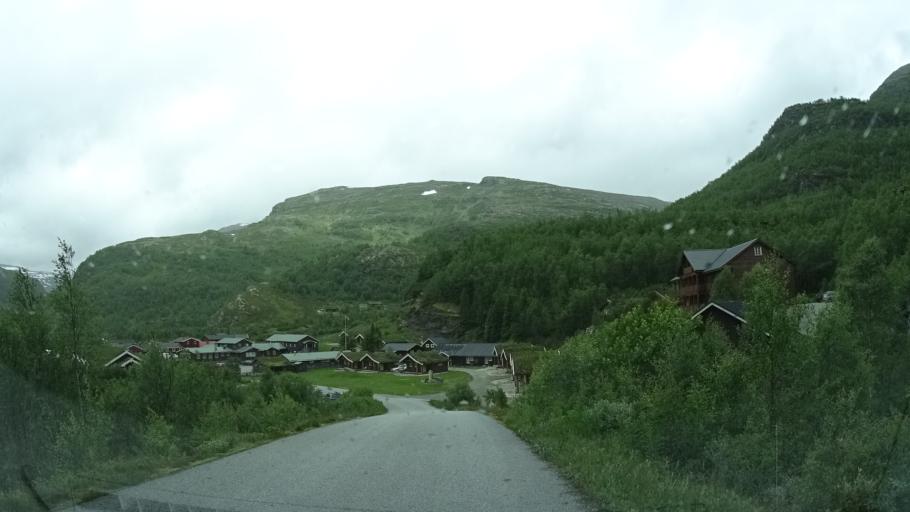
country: NO
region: Sogn og Fjordane
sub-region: Laerdal
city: Laerdalsoyri
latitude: 60.8279
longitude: 7.5085
